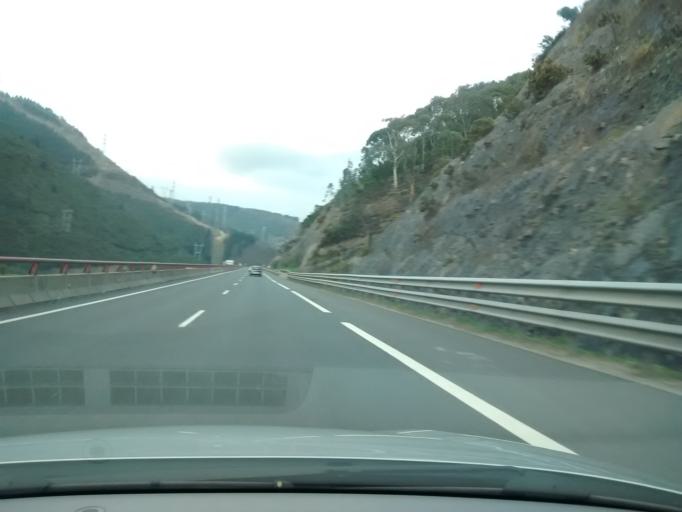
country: ES
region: Basque Country
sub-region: Bizkaia
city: Gordexola
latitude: 43.2092
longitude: -3.0393
